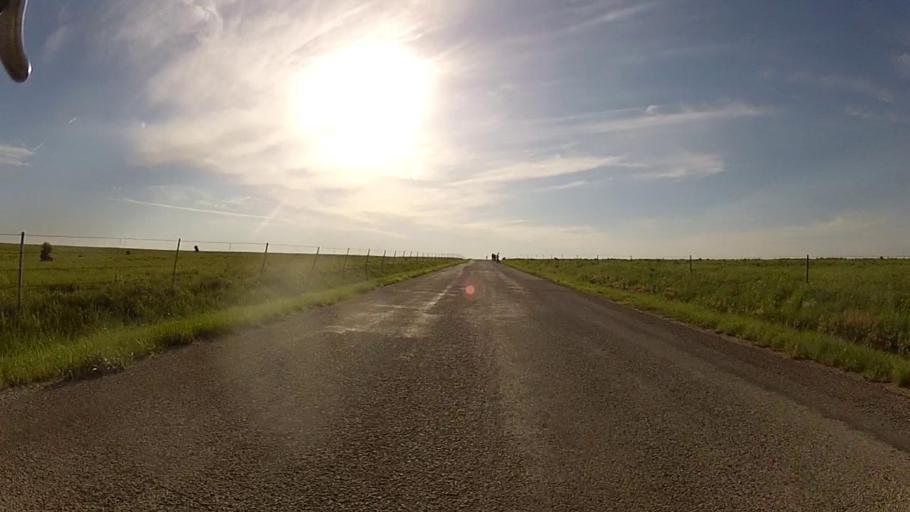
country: US
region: Kansas
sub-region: Cowley County
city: Arkansas City
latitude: 37.0486
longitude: -96.8500
